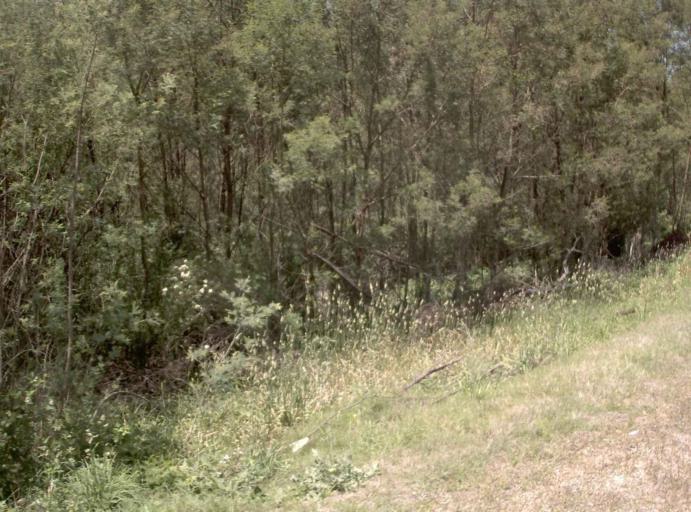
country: AU
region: Victoria
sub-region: East Gippsland
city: Bairnsdale
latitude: -37.5005
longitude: 147.8419
